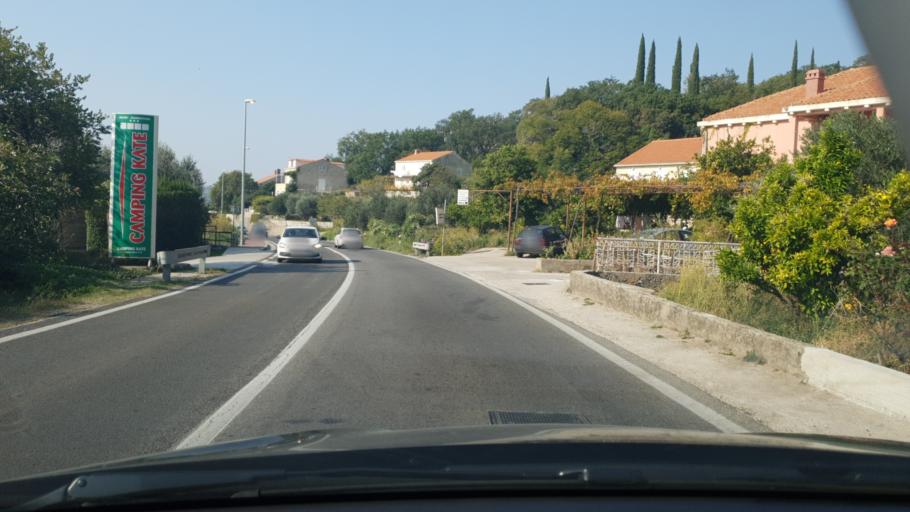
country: HR
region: Dubrovacko-Neretvanska
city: Cibaca
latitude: 42.6249
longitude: 18.2087
